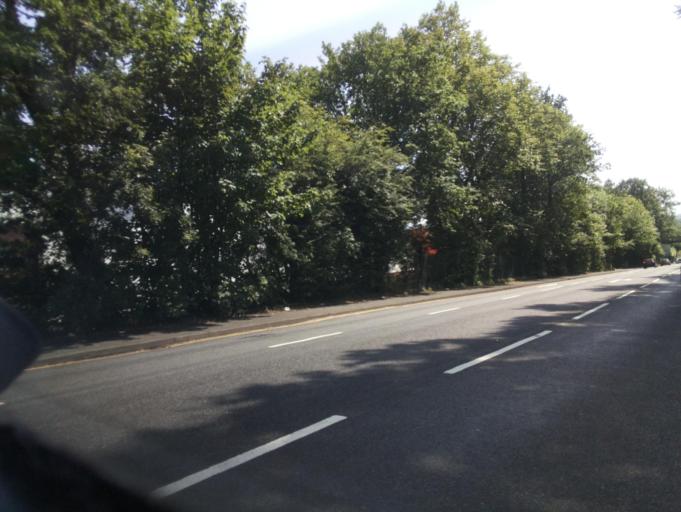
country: GB
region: Wales
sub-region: Caerphilly County Borough
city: Pengam
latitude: 51.6732
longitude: -3.2251
